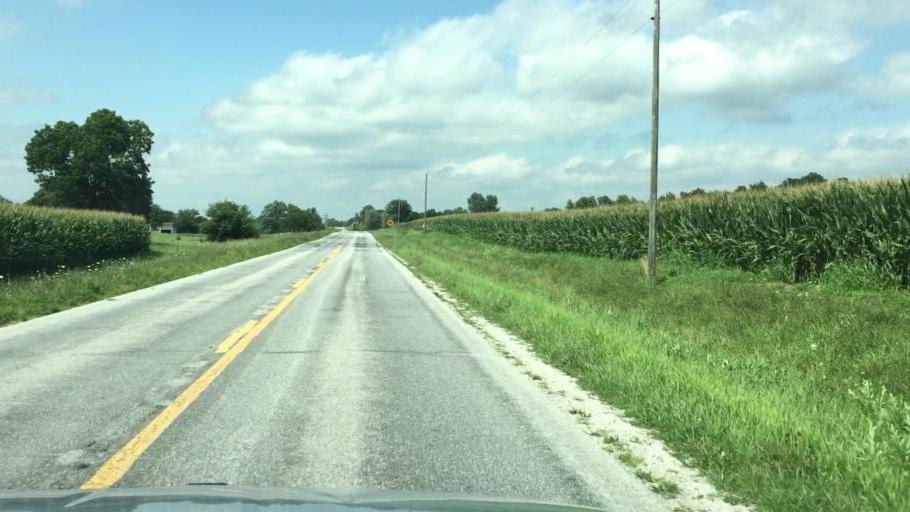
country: US
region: Illinois
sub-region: Hancock County
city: Nauvoo
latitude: 40.5185
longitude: -91.3079
